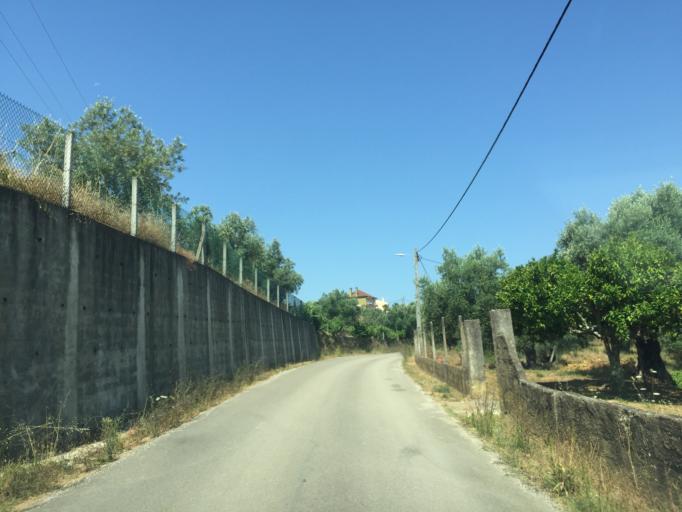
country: PT
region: Santarem
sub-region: Ferreira do Zezere
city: Ferreira do Zezere
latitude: 39.6066
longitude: -8.2842
